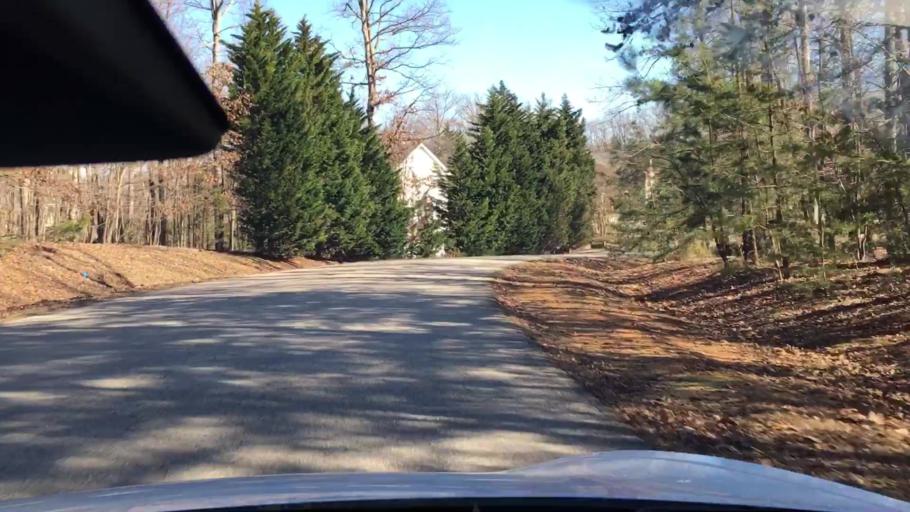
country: US
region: Virginia
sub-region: Chesterfield County
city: Bon Air
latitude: 37.5330
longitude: -77.6138
